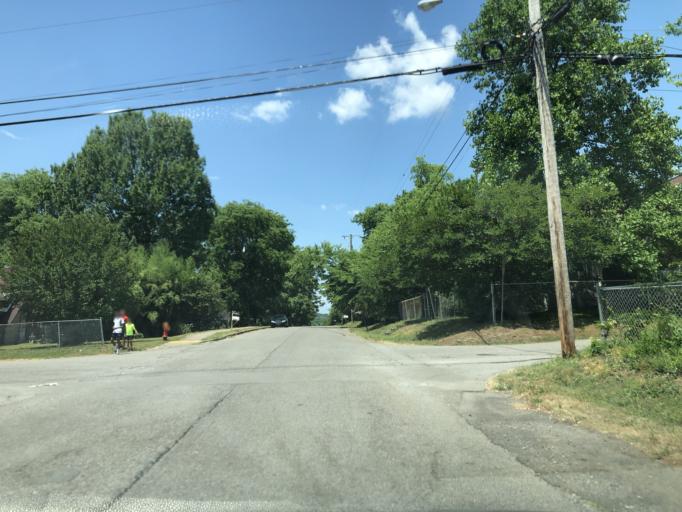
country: US
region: Tennessee
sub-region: Davidson County
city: Goodlettsville
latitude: 36.2663
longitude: -86.7050
